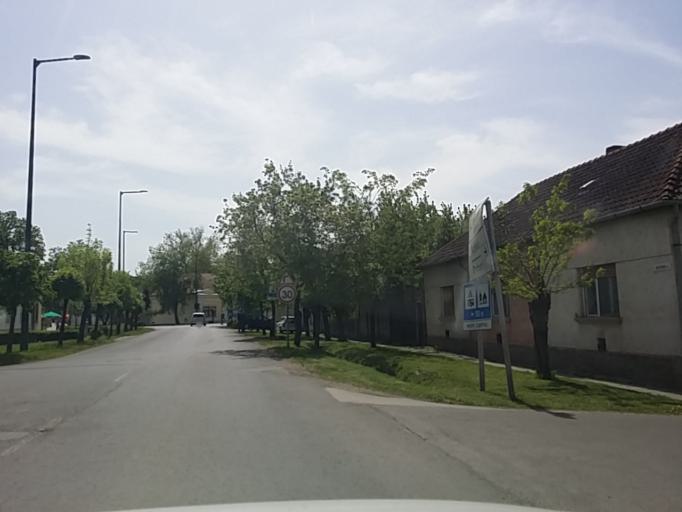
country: HU
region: Bekes
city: Gyula
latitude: 46.6476
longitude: 21.2842
